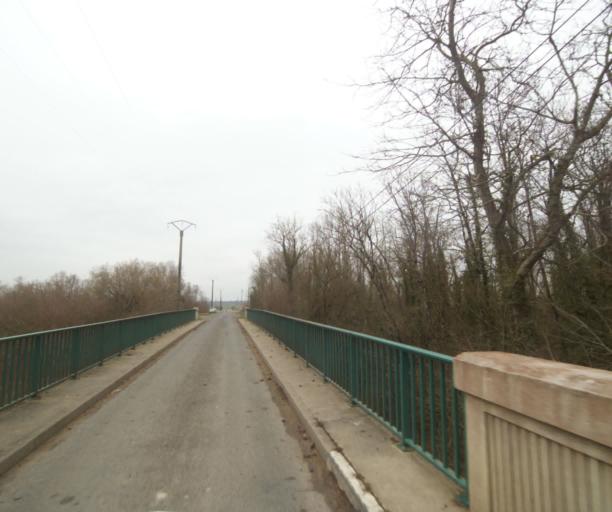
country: FR
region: Champagne-Ardenne
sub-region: Departement de la Haute-Marne
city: Villiers-en-Lieu
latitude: 48.6415
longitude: 4.7678
